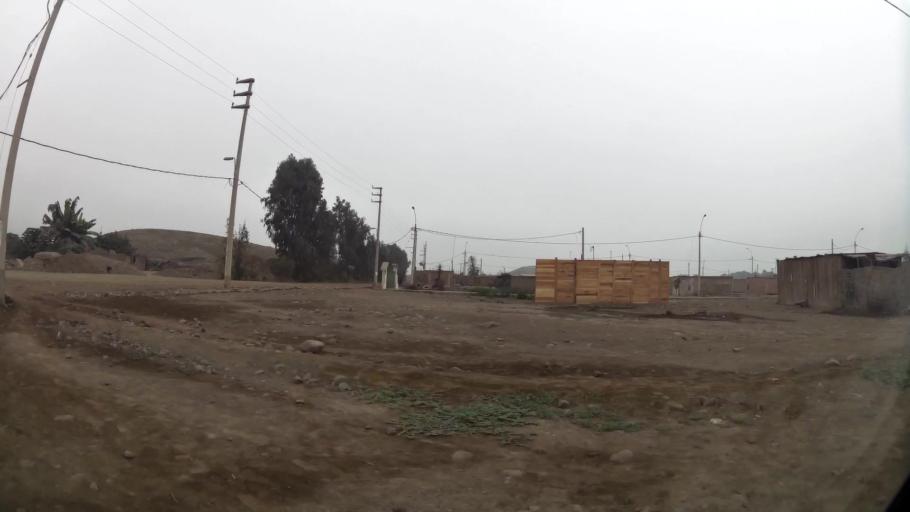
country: PE
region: Lima
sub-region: Lima
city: Carabayllo
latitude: -11.8589
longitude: -77.0170
